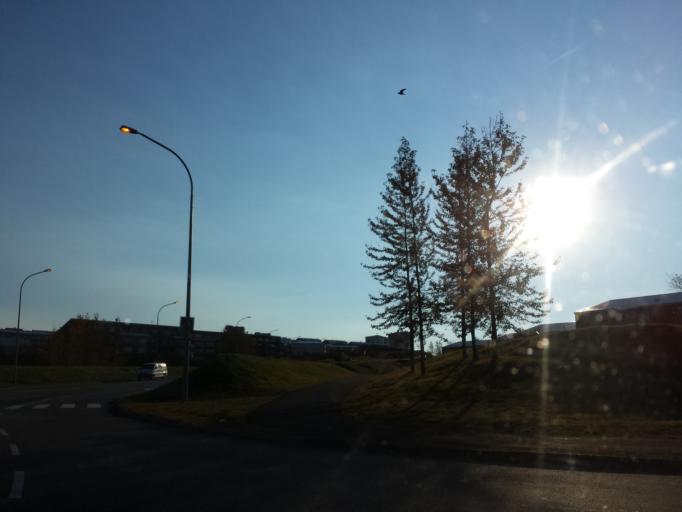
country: IS
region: Capital Region
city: Kopavogur
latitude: 64.0993
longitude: -21.8733
